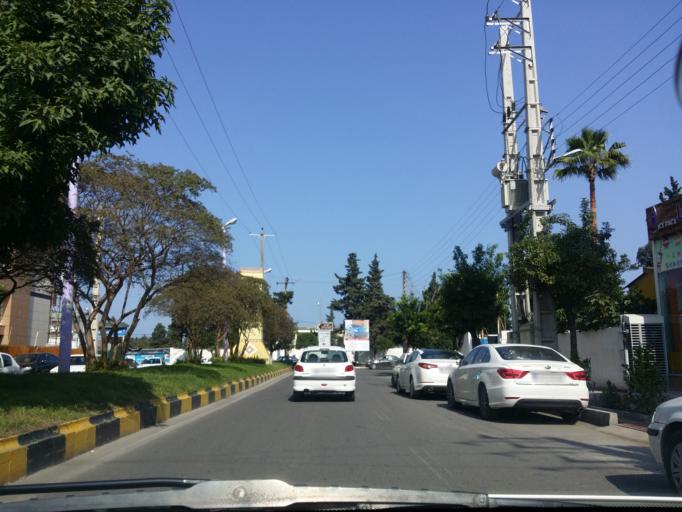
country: IR
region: Mazandaran
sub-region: Nowshahr
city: Nowshahr
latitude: 36.6533
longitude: 51.4954
